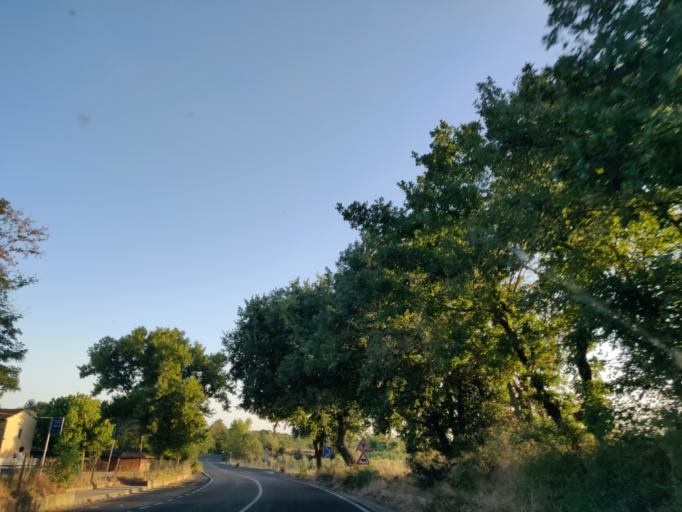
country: IT
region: Latium
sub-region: Provincia di Viterbo
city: Canino
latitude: 42.4137
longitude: 11.7009
